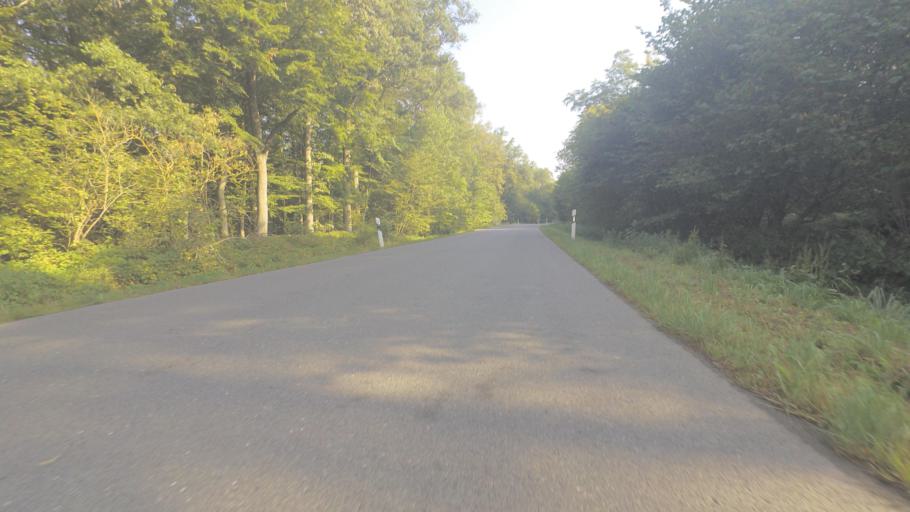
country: DE
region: Mecklenburg-Vorpommern
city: Grimmen
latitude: 54.1426
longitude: 13.0661
